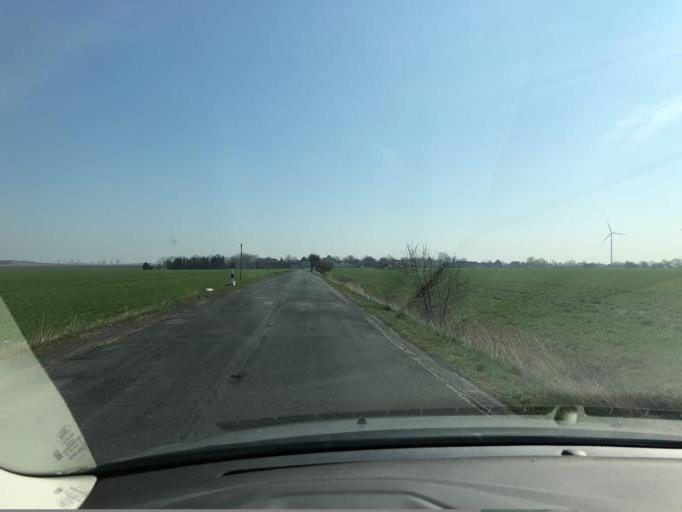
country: DE
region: Saxony
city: Rackwitz
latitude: 51.4243
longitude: 12.4109
